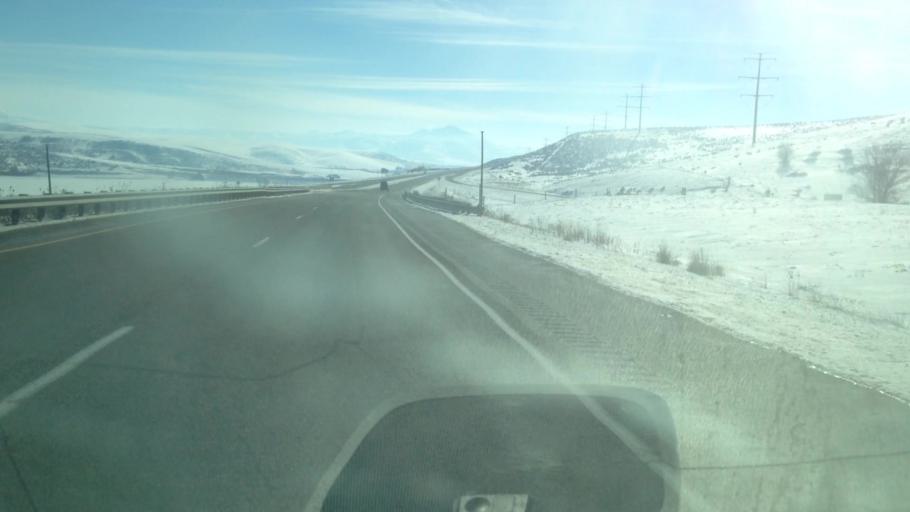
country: US
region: Idaho
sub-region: Oneida County
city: Malad City
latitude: 42.3054
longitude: -112.2100
